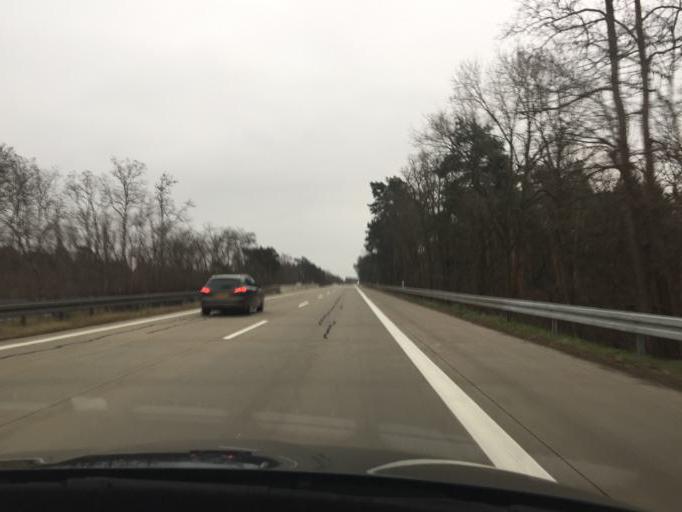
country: DE
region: Brandenburg
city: Lubbenau
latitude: 51.8220
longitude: 14.0103
